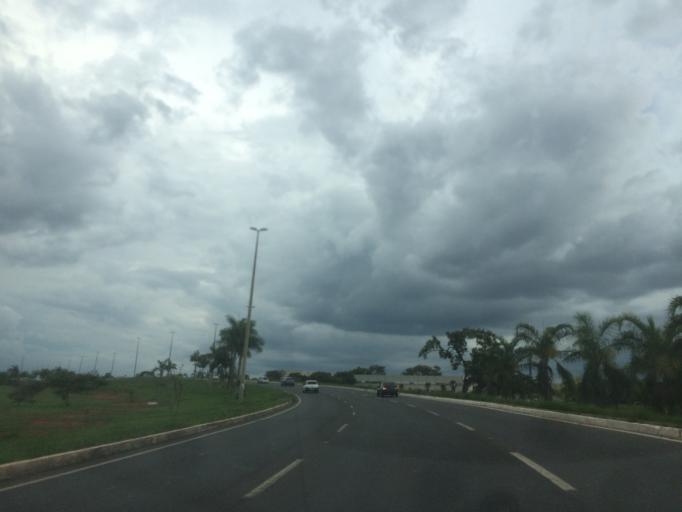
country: BR
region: Federal District
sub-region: Brasilia
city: Brasilia
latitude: -15.7907
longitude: -47.8590
